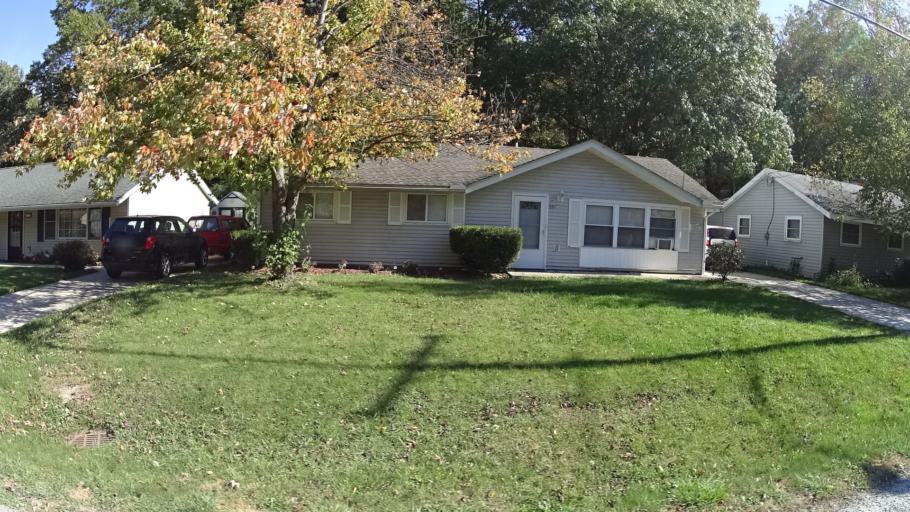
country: US
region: Ohio
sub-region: Lorain County
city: Vermilion-on-the-Lake
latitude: 41.4215
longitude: -82.3256
